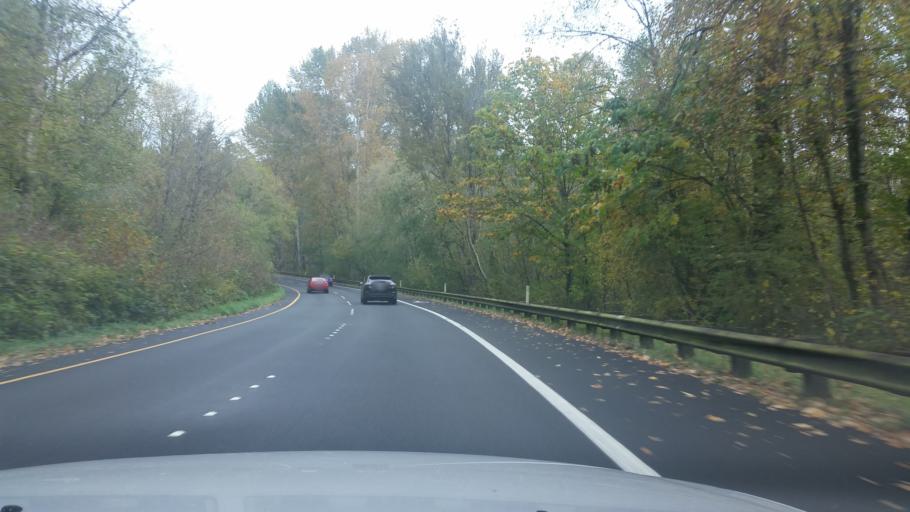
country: US
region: Washington
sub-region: King County
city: Newport
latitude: 47.5972
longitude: -122.1647
